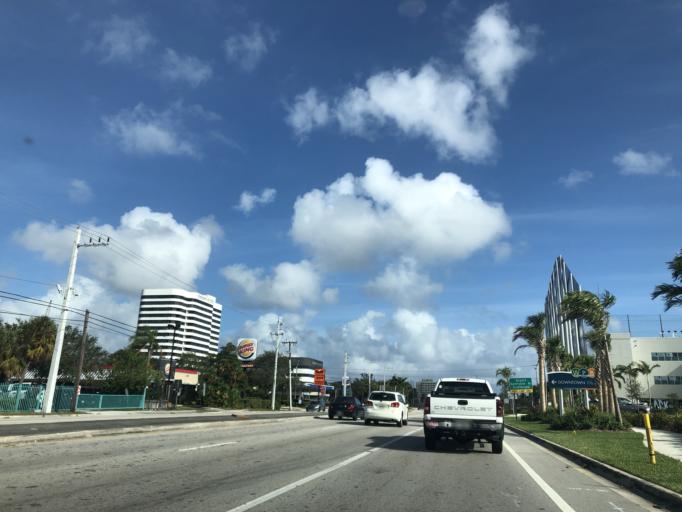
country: US
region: Florida
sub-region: Palm Beach County
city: West Palm Beach
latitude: 26.6909
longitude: -80.0787
